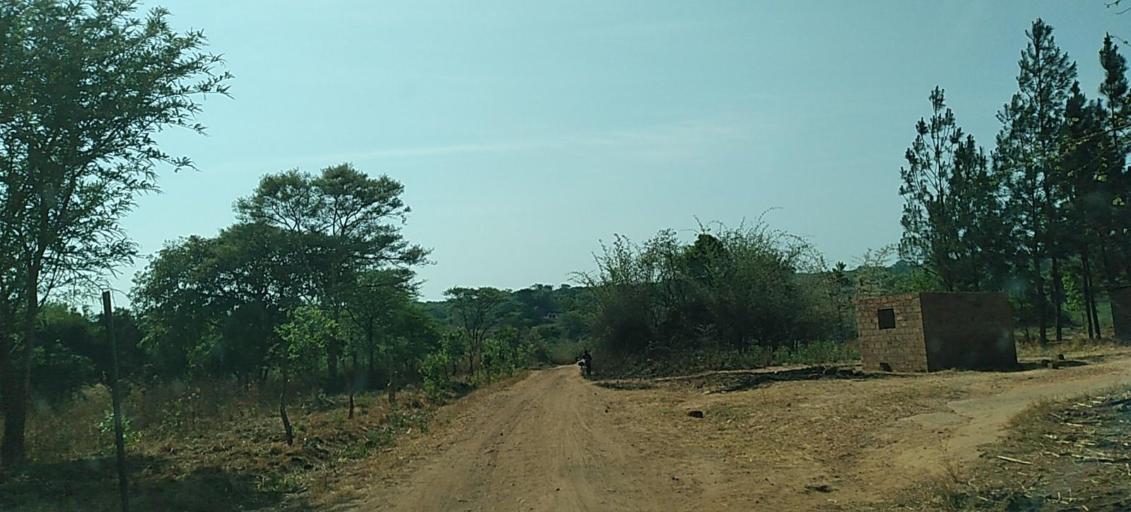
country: ZM
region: Copperbelt
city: Luanshya
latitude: -13.1910
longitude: 28.4778
